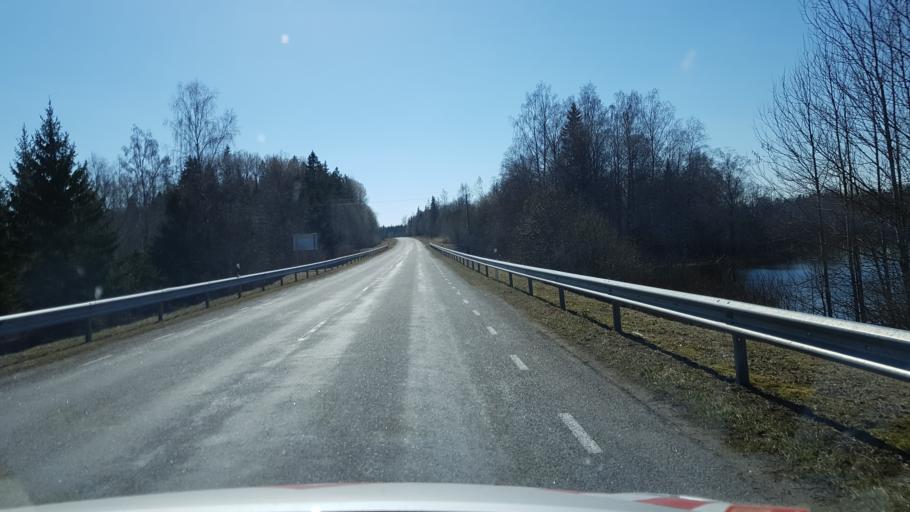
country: EE
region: Laeaene-Virumaa
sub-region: Tamsalu vald
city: Tamsalu
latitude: 59.1597
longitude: 26.0780
